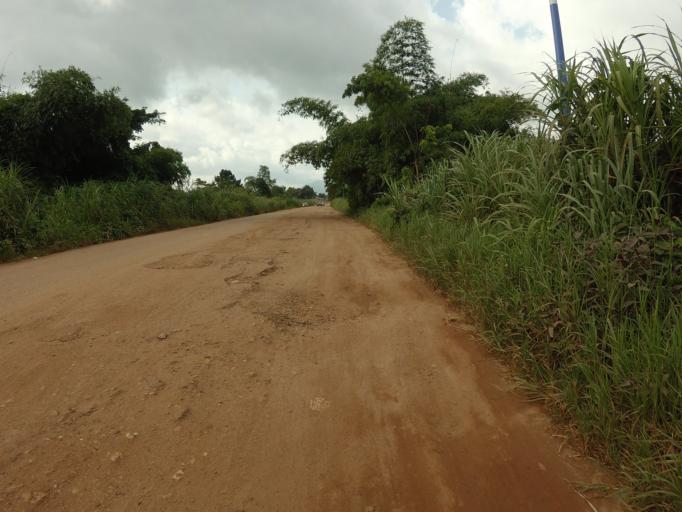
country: GH
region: Volta
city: Hohoe
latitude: 7.1266
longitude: 0.4606
